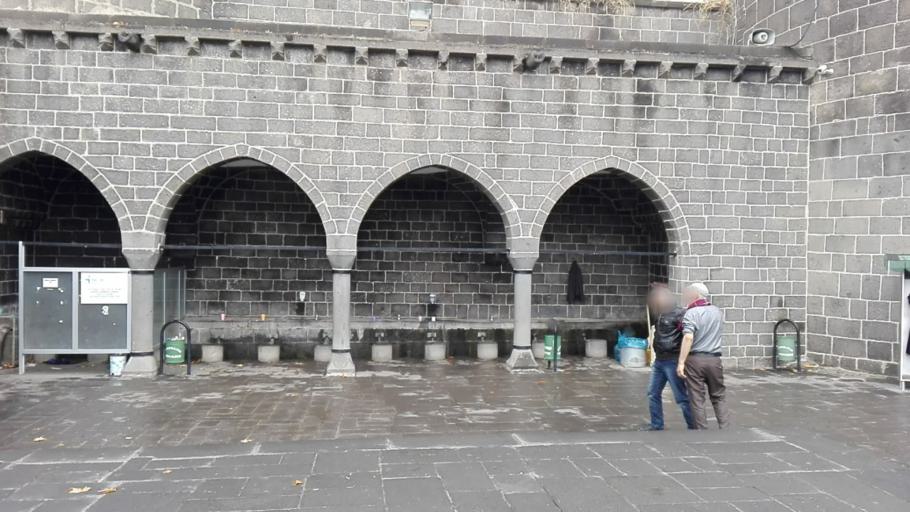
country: TR
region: Diyarbakir
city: Sur
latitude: 37.9150
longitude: 40.2419
